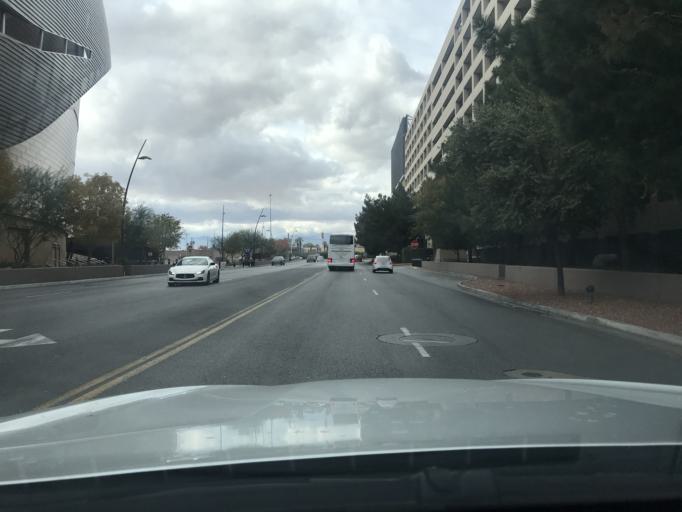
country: US
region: Nevada
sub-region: Clark County
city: Paradise
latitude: 36.1040
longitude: -115.1774
